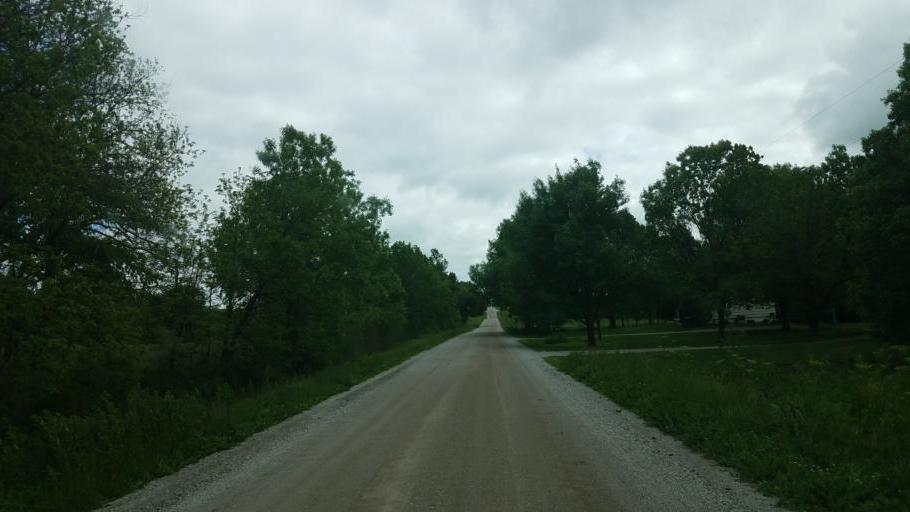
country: US
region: Iowa
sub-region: Decatur County
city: Lamoni
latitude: 40.6149
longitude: -93.8439
